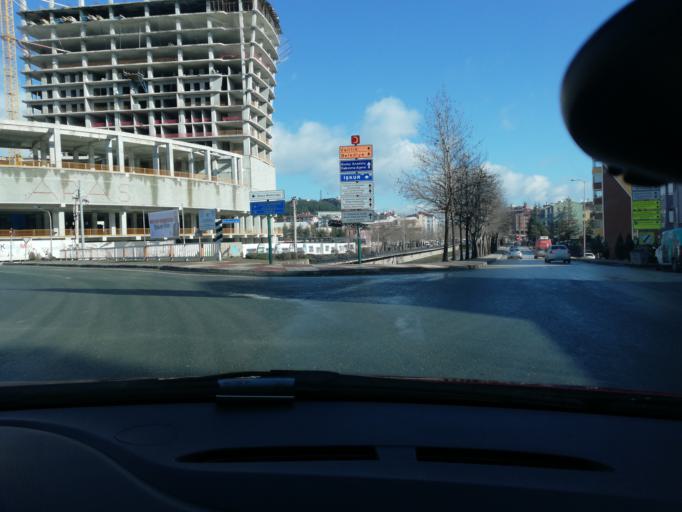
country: TR
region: Kastamonu
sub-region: Cide
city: Kastamonu
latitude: 41.3630
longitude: 33.7673
